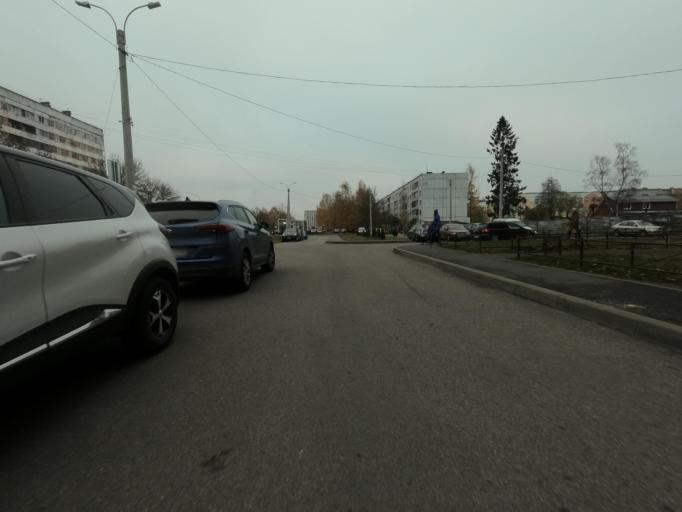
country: RU
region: Leningrad
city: Kirovsk
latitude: 59.8852
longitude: 30.9928
